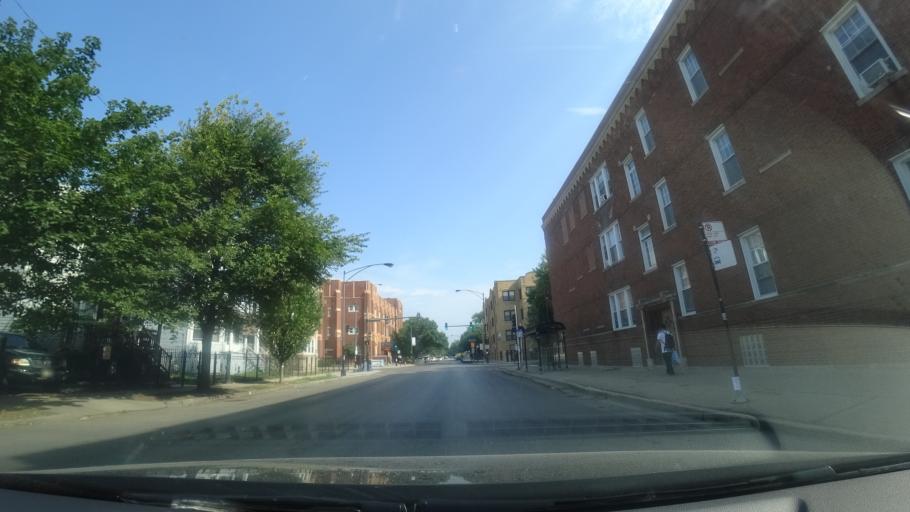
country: US
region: Illinois
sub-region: Cook County
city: Lincolnwood
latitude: 41.9642
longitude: -87.7132
